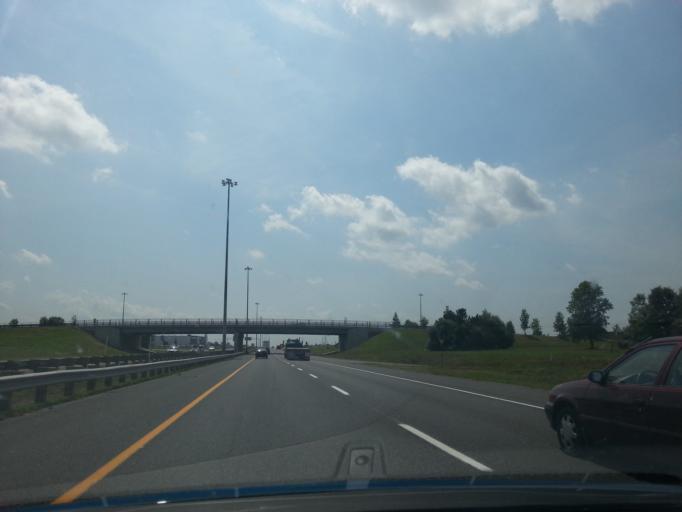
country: CA
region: Quebec
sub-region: Centre-du-Quebec
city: Drummondville
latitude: 45.9022
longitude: -72.5251
